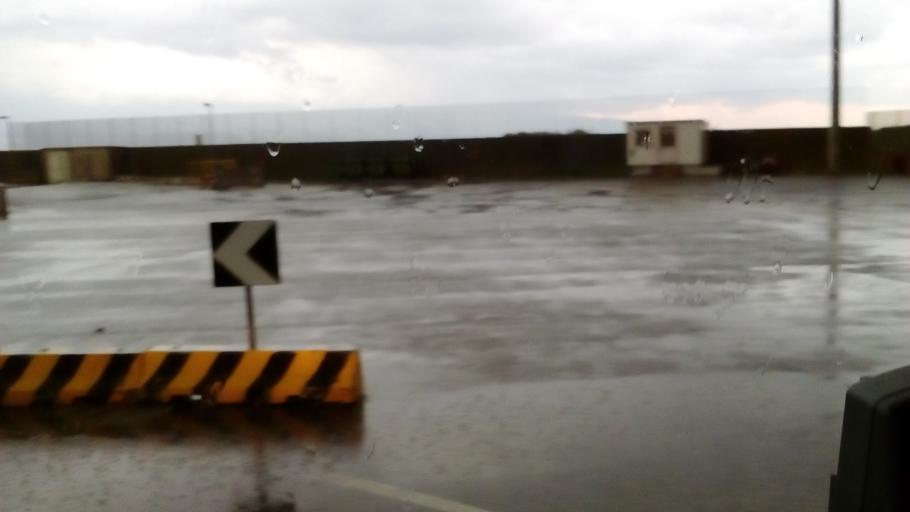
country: IT
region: Sicily
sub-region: Messina
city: Larderia
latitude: 38.1314
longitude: 15.5226
